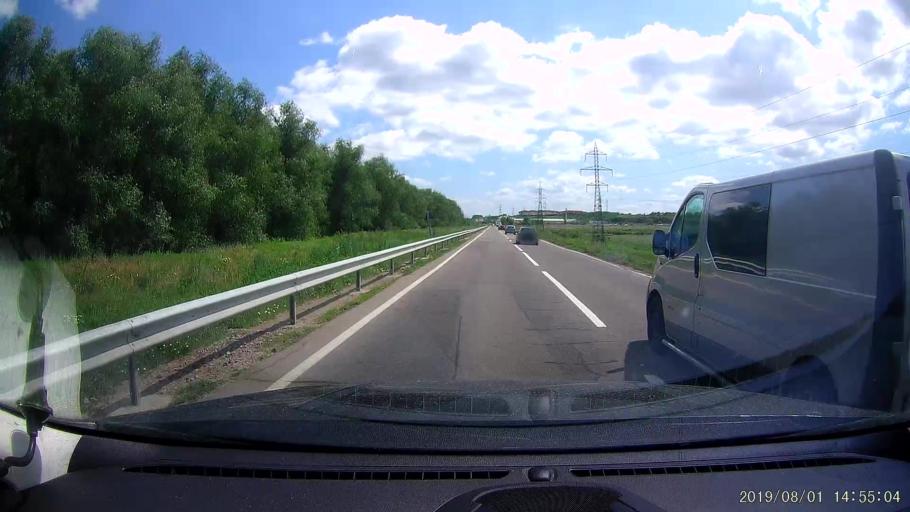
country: RO
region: Braila
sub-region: Municipiul Braila
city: Braila
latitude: 45.3088
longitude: 27.9836
